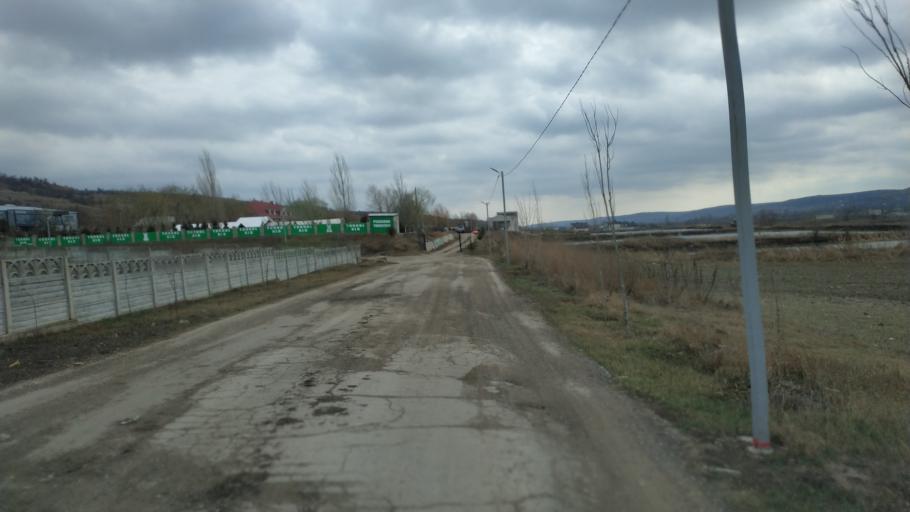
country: MD
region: Laloveni
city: Ialoveni
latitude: 46.8786
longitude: 28.7685
